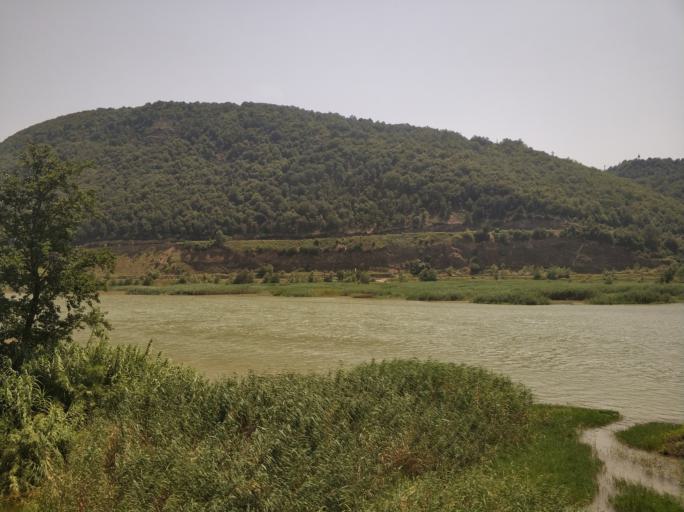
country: IR
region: Gilan
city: Pa'in-e Bazar-e Rudbar
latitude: 36.9766
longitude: 49.5543
